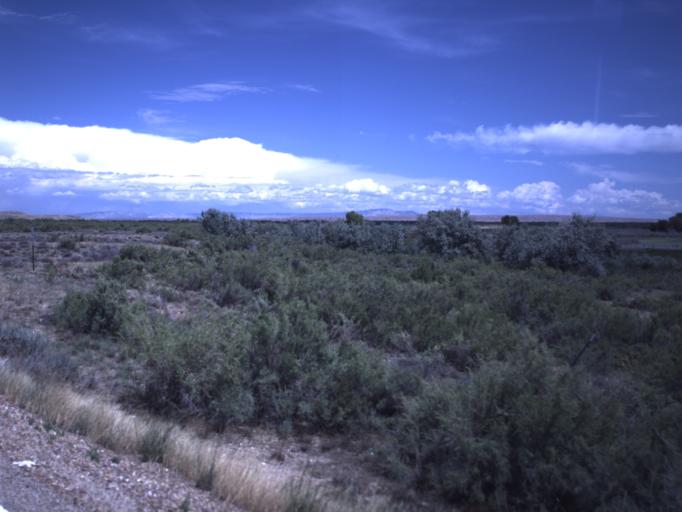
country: US
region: Utah
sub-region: Uintah County
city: Naples
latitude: 40.1085
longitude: -109.6706
